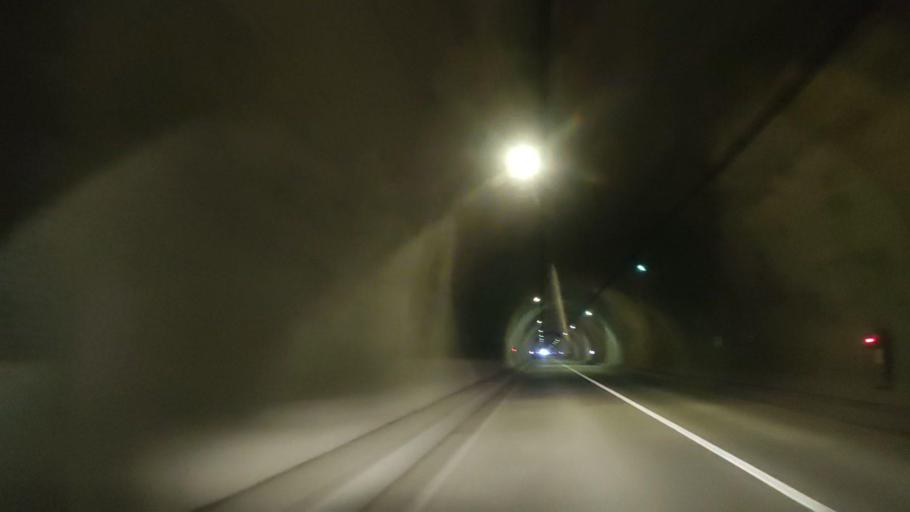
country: JP
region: Hokkaido
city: Iwamizawa
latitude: 43.0326
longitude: 142.0904
